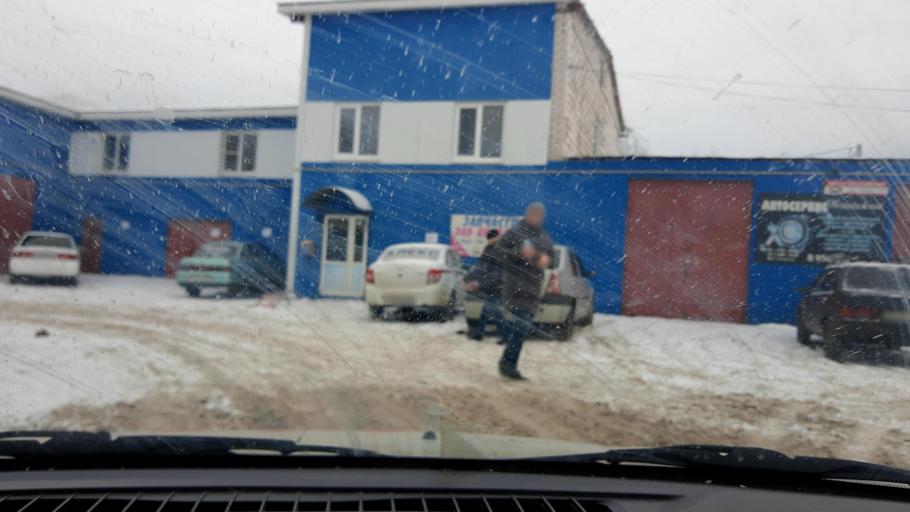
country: RU
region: Nizjnij Novgorod
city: Gorodets
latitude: 56.6581
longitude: 43.4847
